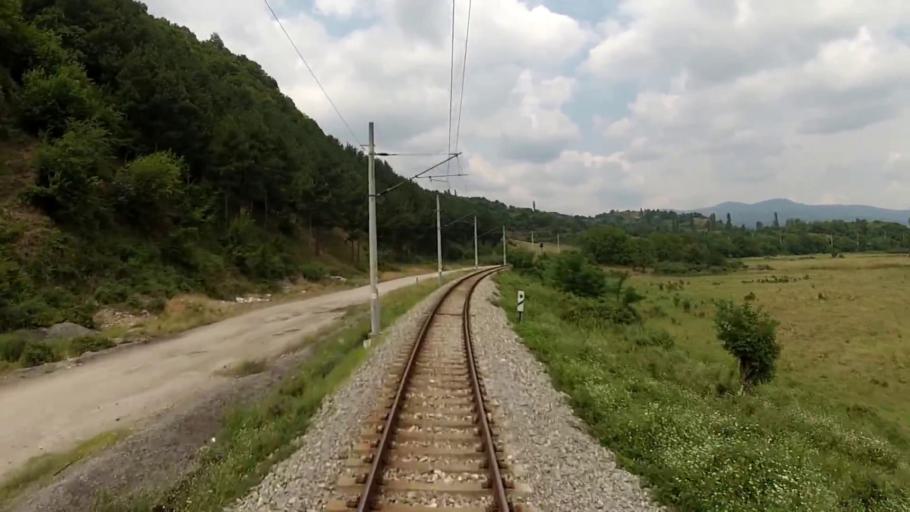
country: BG
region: Blagoevgrad
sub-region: Obshtina Simitli
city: Simitli
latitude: 41.8452
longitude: 23.1477
